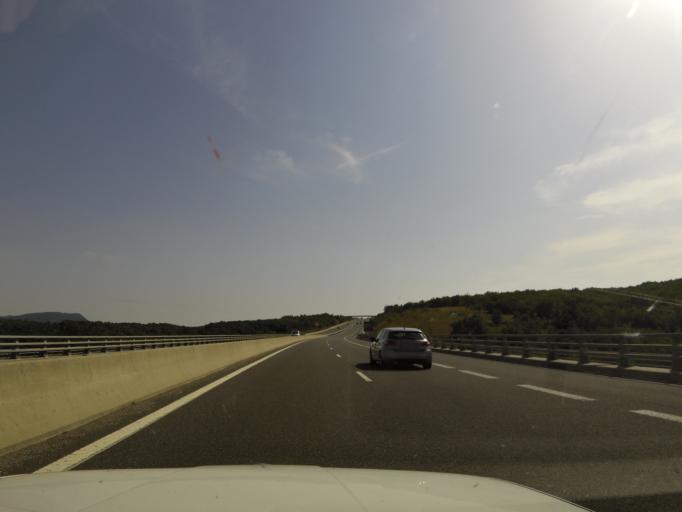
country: FR
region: Midi-Pyrenees
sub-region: Departement de l'Aveyron
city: Millau
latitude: 44.1956
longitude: 3.0646
